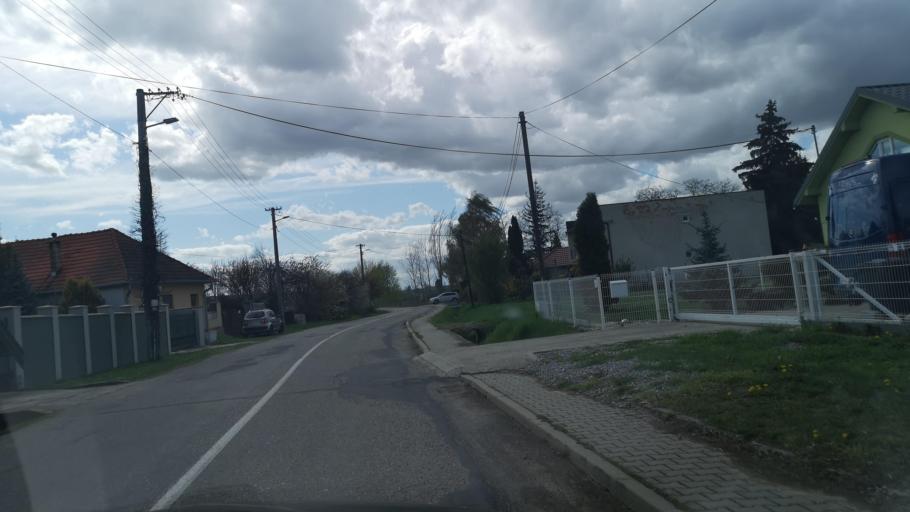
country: SK
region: Nitriansky
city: Zlate Moravce
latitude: 48.3169
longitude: 18.3556
